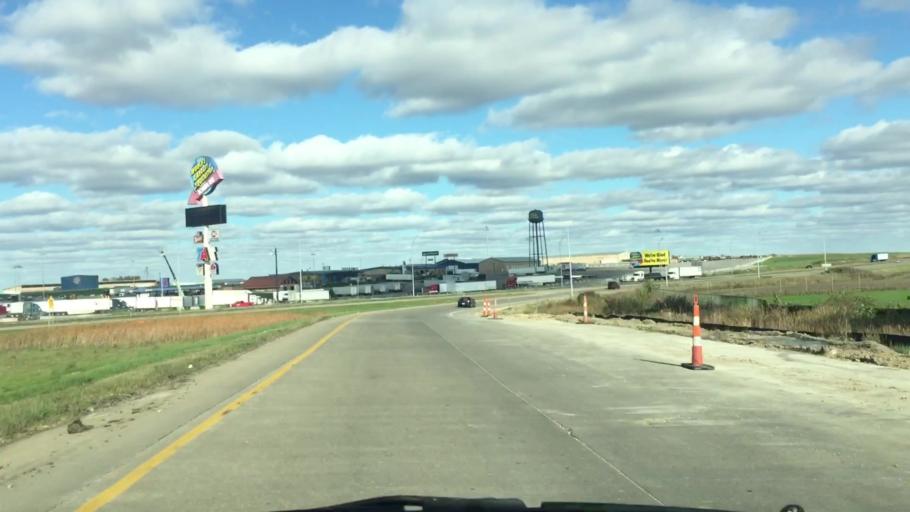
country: US
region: Iowa
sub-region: Scott County
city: Walcott
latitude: 41.6152
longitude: -90.7826
